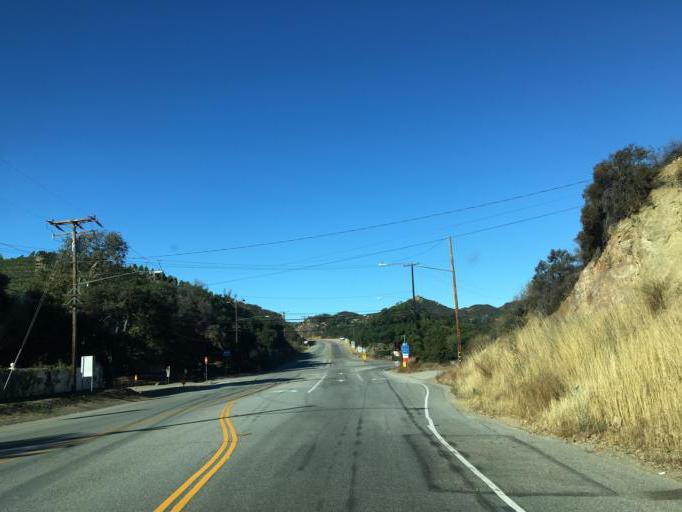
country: US
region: California
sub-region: Los Angeles County
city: Westlake Village
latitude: 34.0971
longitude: -118.8117
